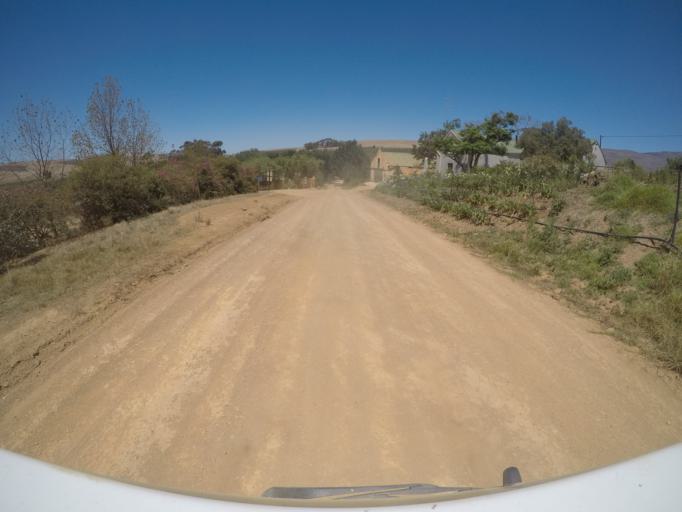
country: ZA
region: Western Cape
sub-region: Overberg District Municipality
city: Grabouw
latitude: -34.0939
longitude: 19.1968
